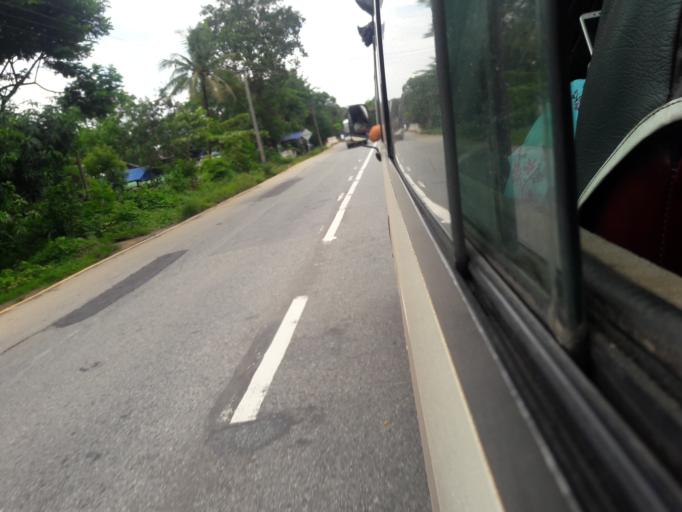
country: MM
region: Bago
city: Nyaunglebin
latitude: 17.8227
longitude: 96.6735
